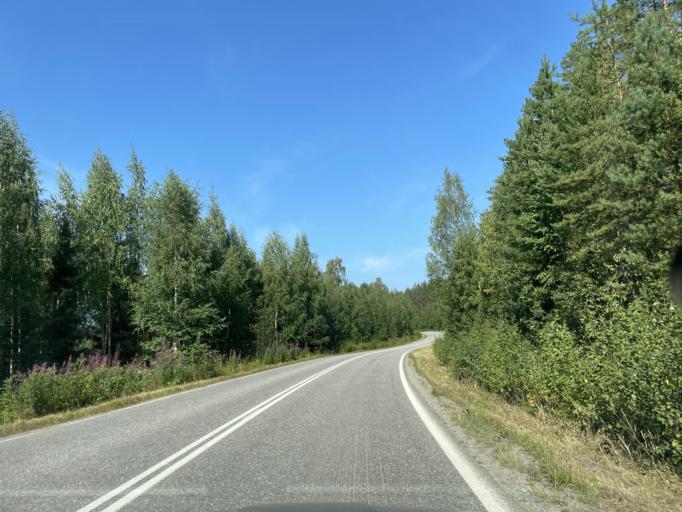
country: FI
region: Central Finland
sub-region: Saarijaervi-Viitasaari
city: Pihtipudas
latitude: 63.3714
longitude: 25.6156
